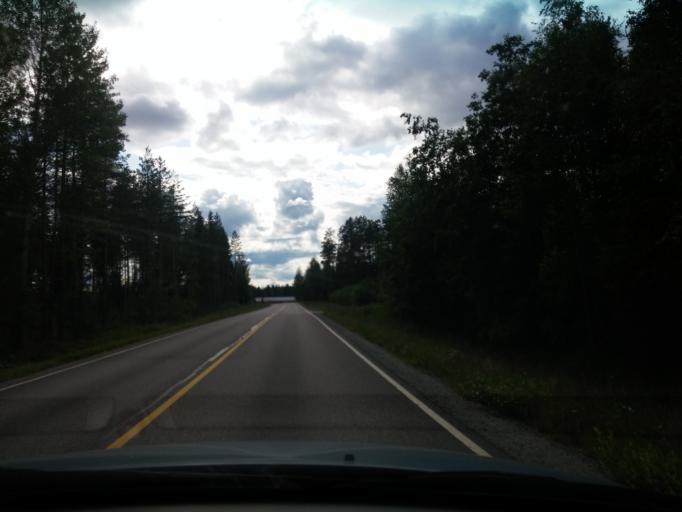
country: FI
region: Central Finland
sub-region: Saarijaervi-Viitasaari
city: Pylkoenmaeki
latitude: 62.6273
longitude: 24.7886
